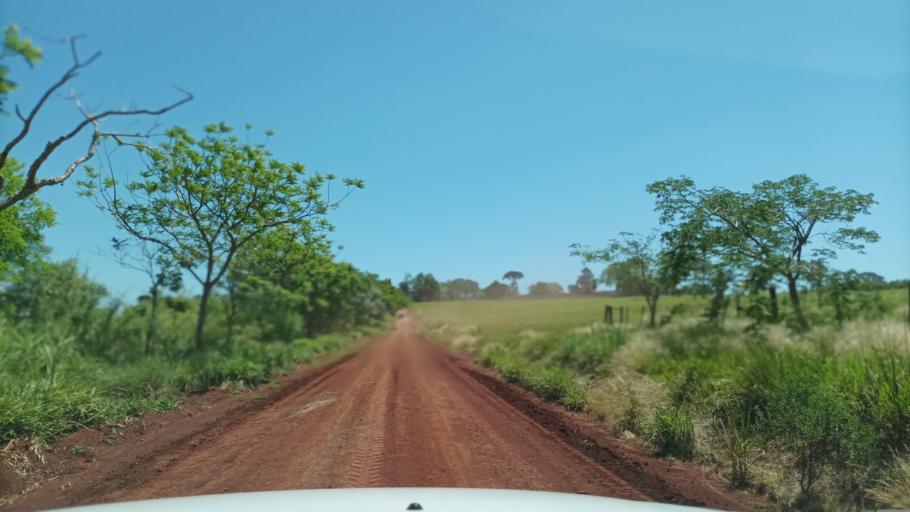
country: AR
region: Misiones
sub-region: Departamento de Apostoles
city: San Jose
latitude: -27.7904
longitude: -55.7118
